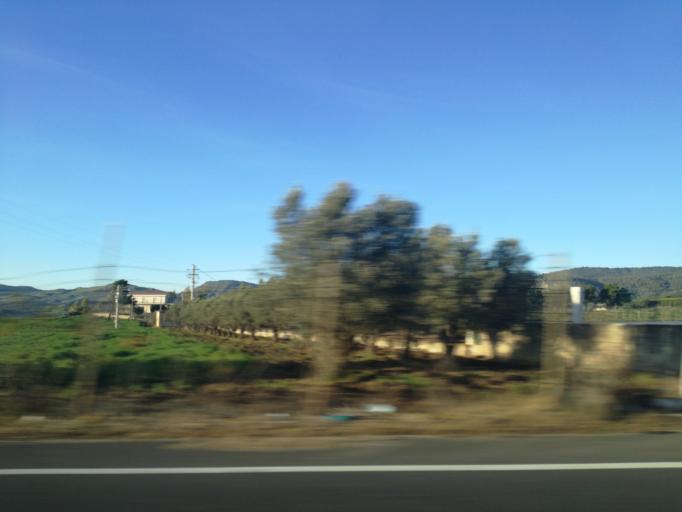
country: IT
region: Sicily
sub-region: Catania
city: San Michele di Ganzaria
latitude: 37.2143
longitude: 14.4075
